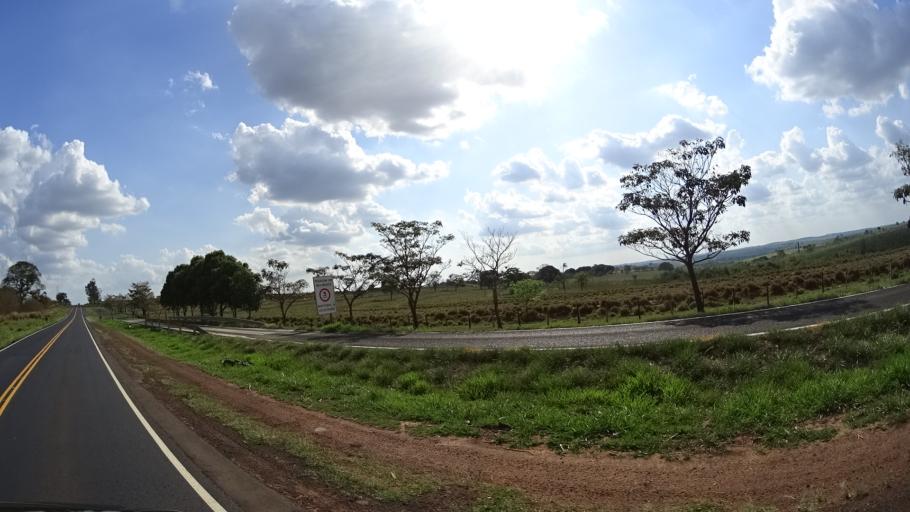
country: BR
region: Sao Paulo
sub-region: Urupes
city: Urupes
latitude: -21.1026
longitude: -49.2633
